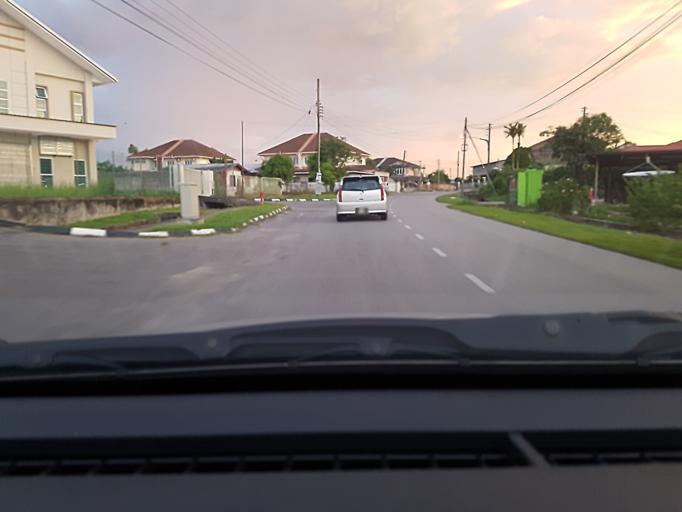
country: MY
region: Sarawak
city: Kuching
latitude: 1.4905
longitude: 110.3218
